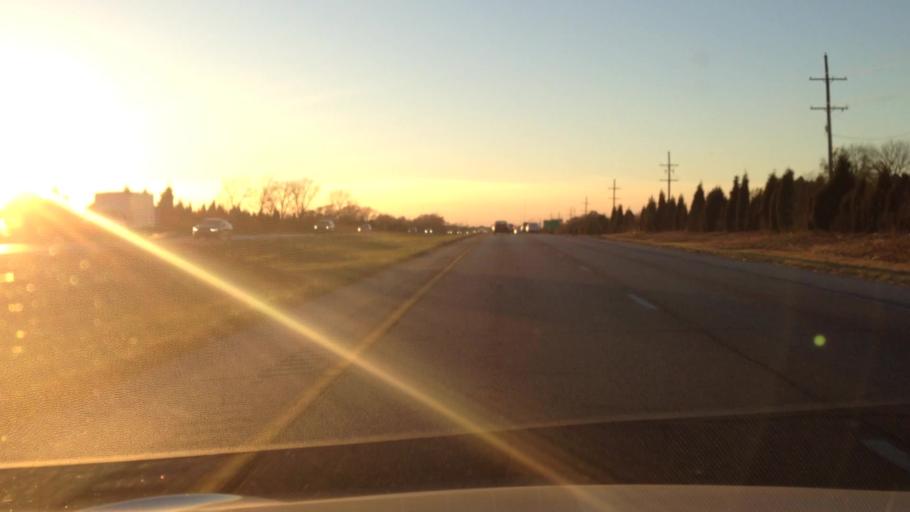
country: US
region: Kansas
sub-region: Johnson County
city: Olathe
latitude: 38.9413
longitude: -94.8355
